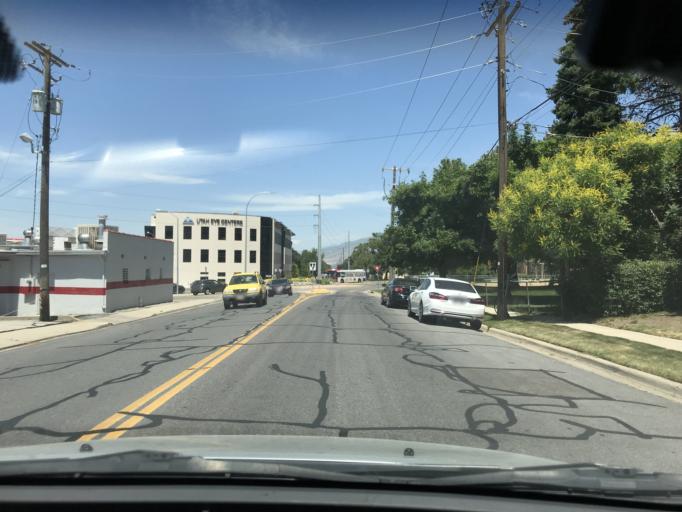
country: US
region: Utah
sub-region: Davis County
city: Woods Cross
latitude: 40.8739
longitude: -111.8857
